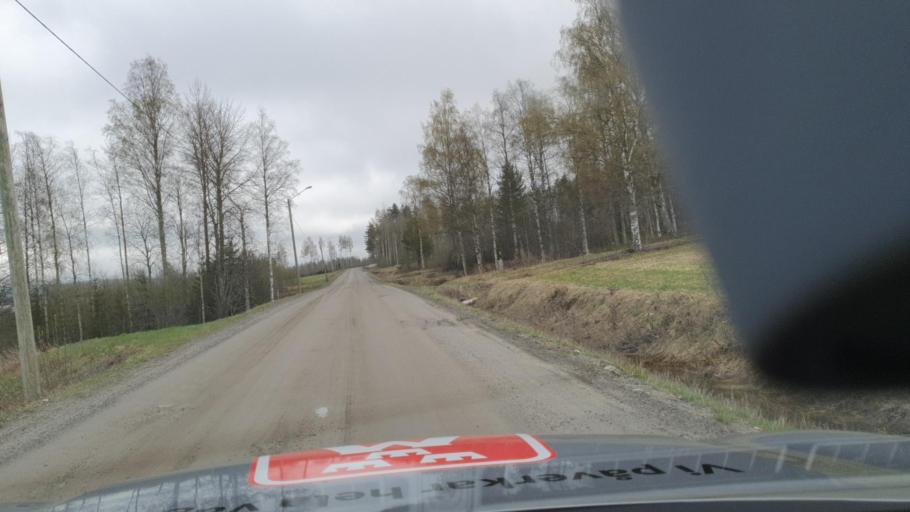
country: SE
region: Vaesterbotten
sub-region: Bjurholms Kommun
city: Bjurholm
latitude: 63.6629
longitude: 19.0222
